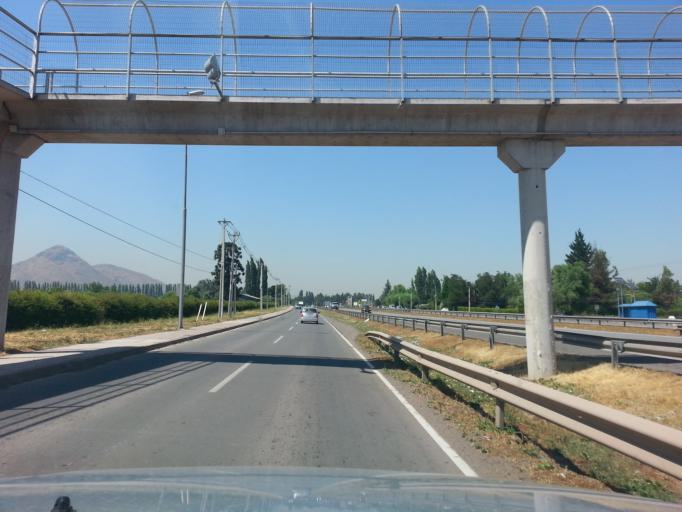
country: CL
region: Santiago Metropolitan
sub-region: Provincia de Chacabuco
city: Chicureo Abajo
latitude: -33.2716
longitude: -70.7006
